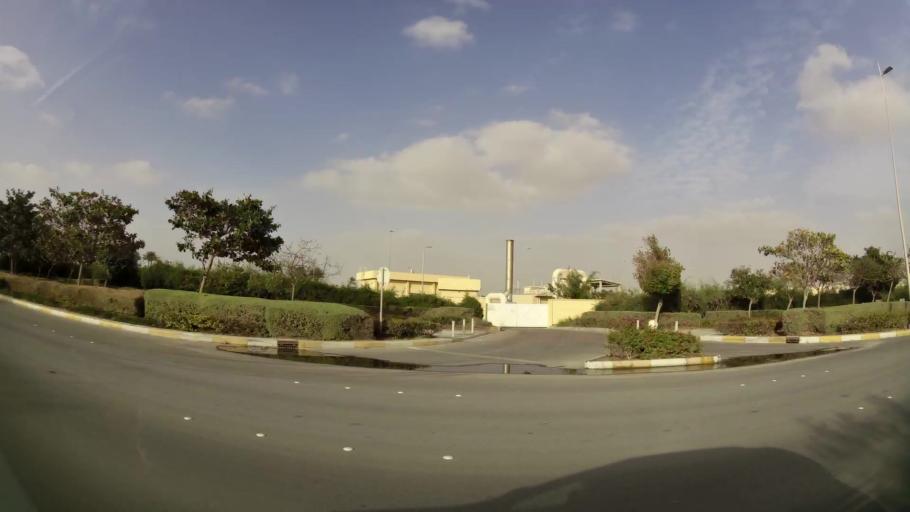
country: AE
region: Abu Dhabi
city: Abu Dhabi
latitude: 24.4996
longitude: 54.5840
